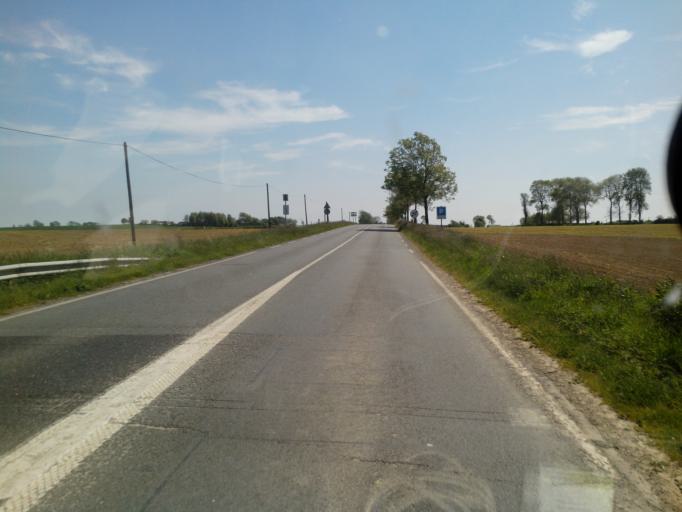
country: FR
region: Nord-Pas-de-Calais
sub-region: Departement du Pas-de-Calais
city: Samer
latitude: 50.6069
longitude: 1.7443
